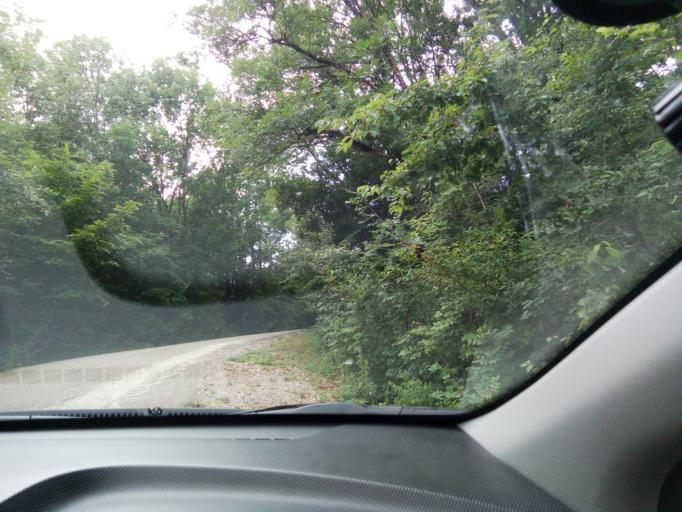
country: RU
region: Krasnodarskiy
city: Apsheronsk
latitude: 44.4549
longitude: 39.8502
